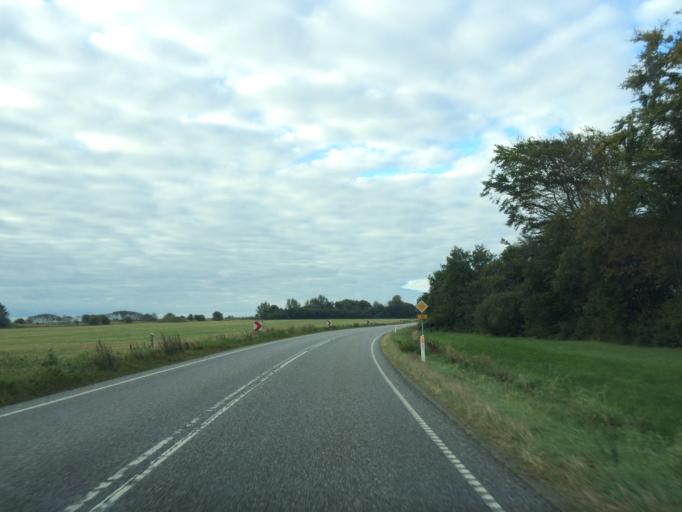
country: DK
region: Central Jutland
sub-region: Ringkobing-Skjern Kommune
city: Skjern
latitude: 55.9908
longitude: 8.5083
